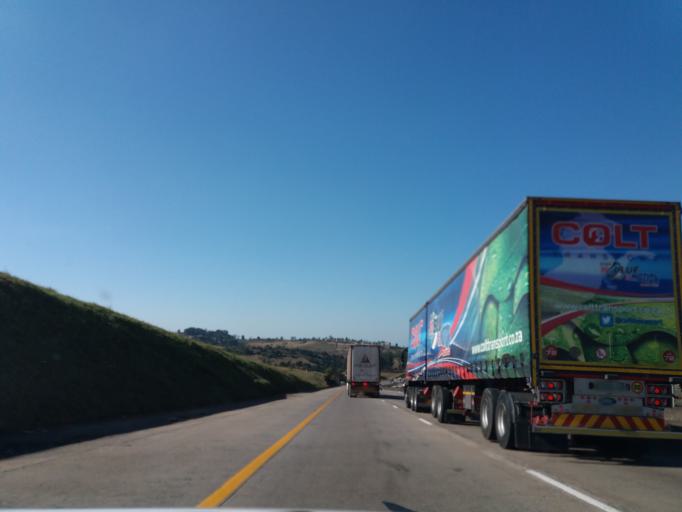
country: ZA
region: KwaZulu-Natal
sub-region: eThekwini Metropolitan Municipality
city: Mpumalanga
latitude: -29.7386
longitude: 30.6394
